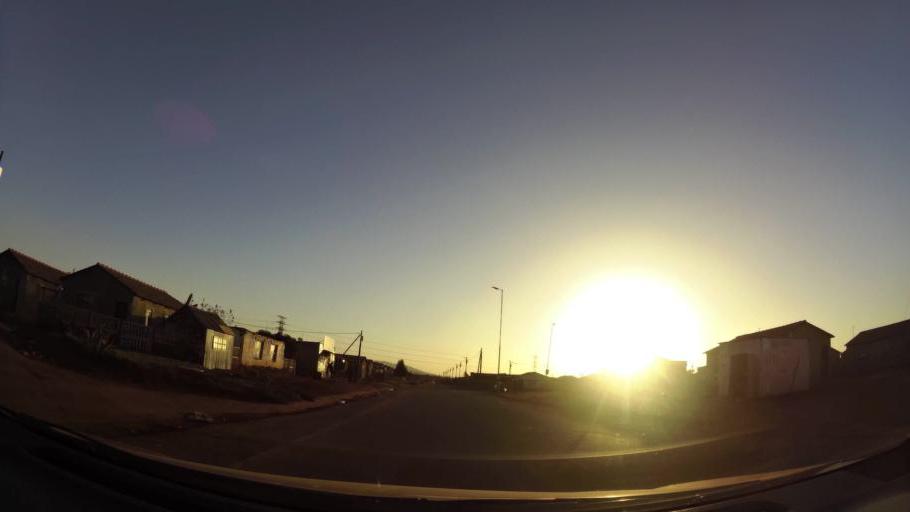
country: ZA
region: North-West
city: Ga-Rankuwa
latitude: -25.6028
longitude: 28.0857
